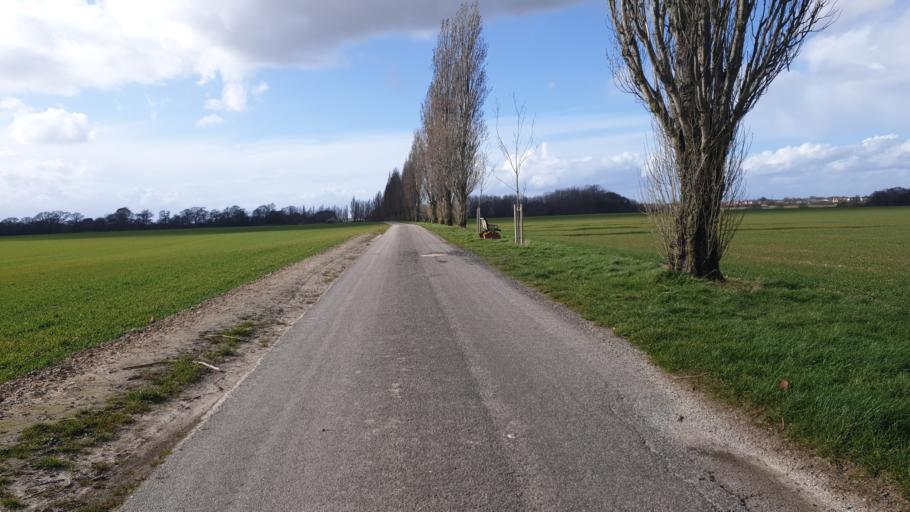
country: GB
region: England
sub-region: Essex
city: Little Clacton
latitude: 51.8498
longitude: 1.1390
